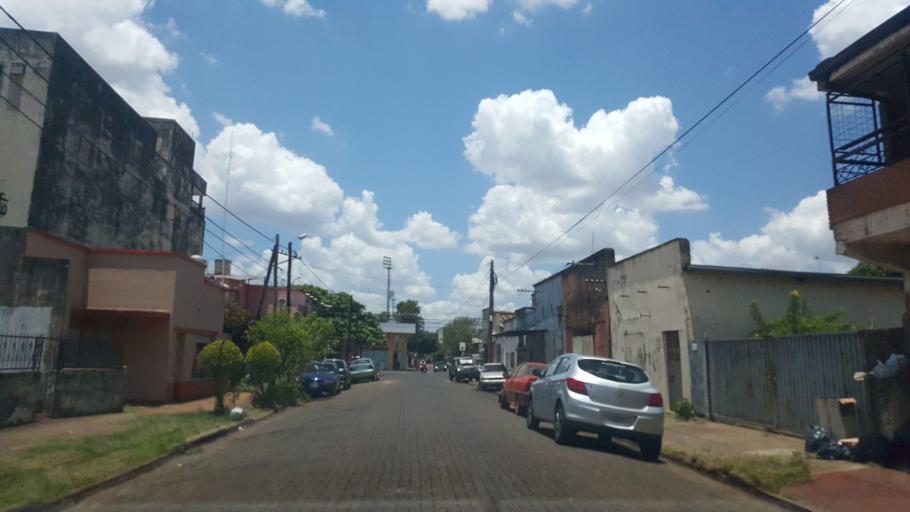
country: AR
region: Misiones
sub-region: Departamento de Capital
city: Posadas
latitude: -27.3858
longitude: -55.9010
